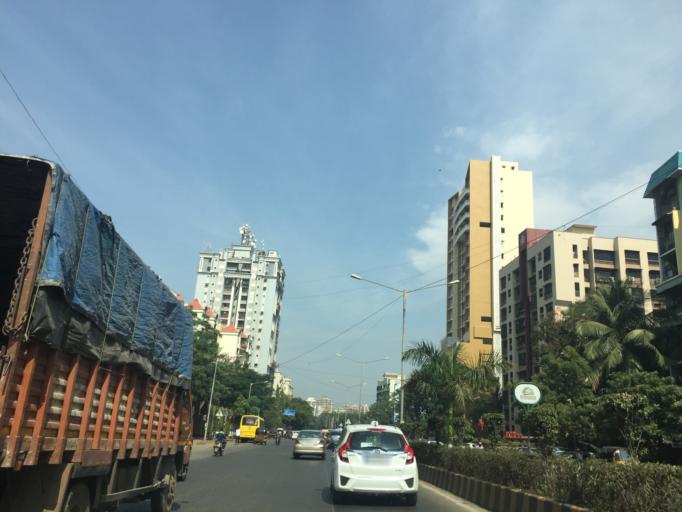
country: IN
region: Maharashtra
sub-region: Mumbai Suburban
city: Borivli
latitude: 19.2264
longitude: 72.8408
